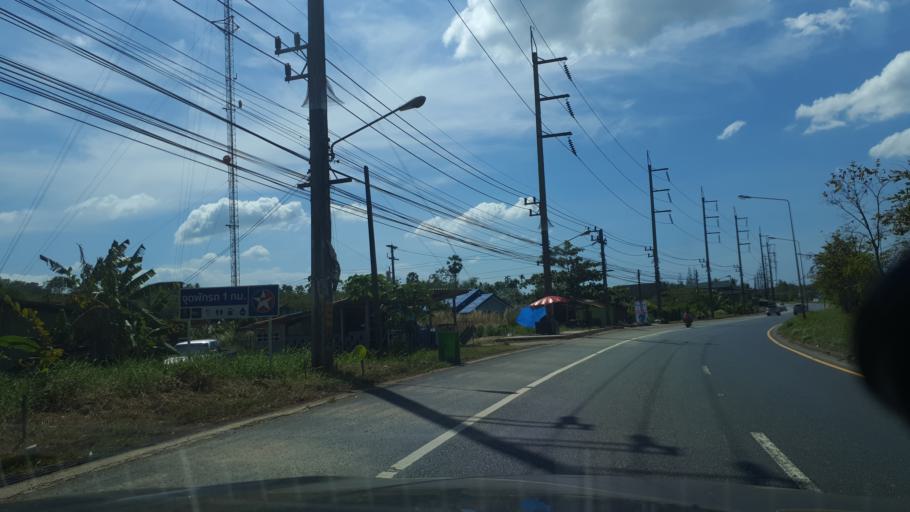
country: TH
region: Phangnga
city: Takua Thung
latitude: 8.2753
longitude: 98.3513
